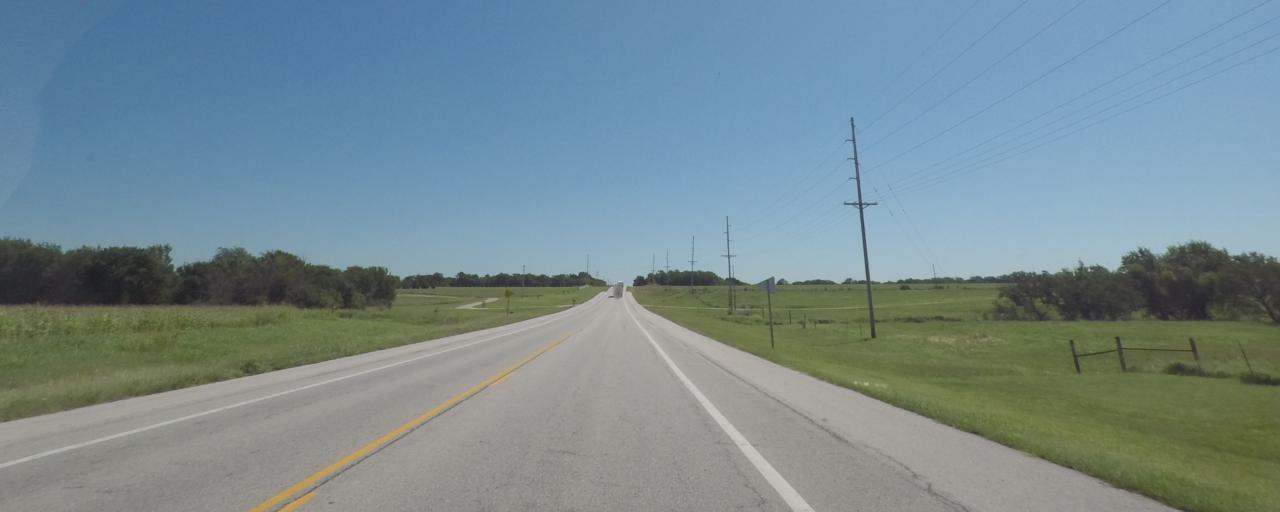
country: US
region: Kansas
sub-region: Sumner County
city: Belle Plaine
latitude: 37.3912
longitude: -97.3788
